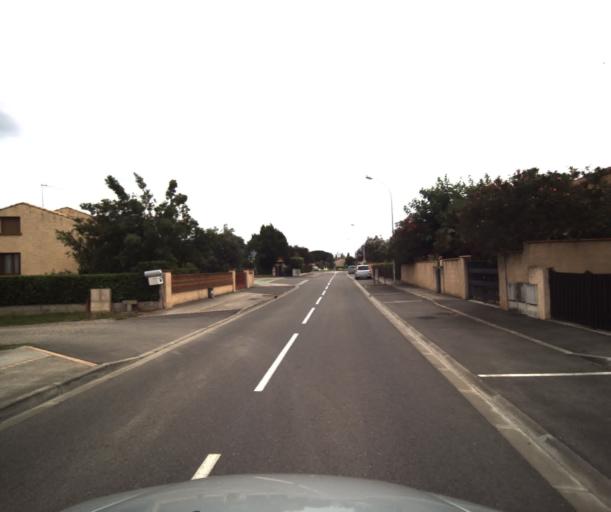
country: FR
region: Midi-Pyrenees
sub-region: Departement de la Haute-Garonne
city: Muret
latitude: 43.4479
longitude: 1.3141
